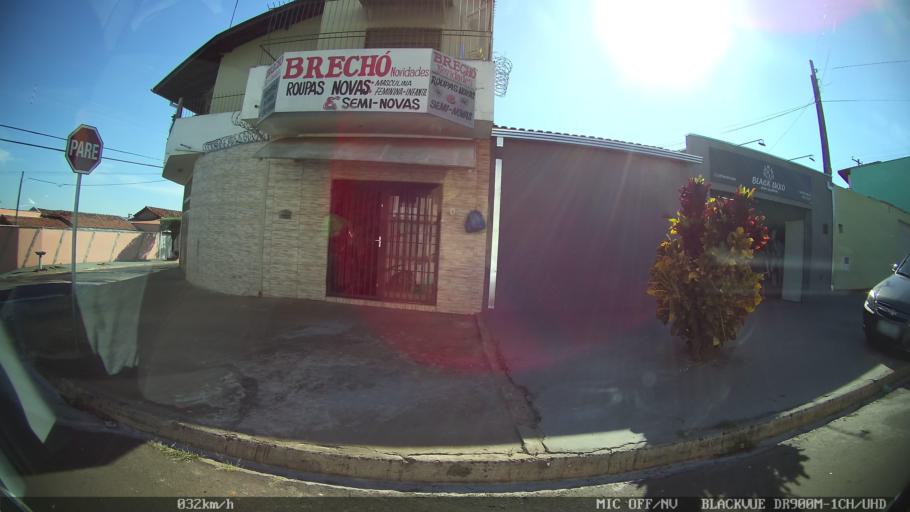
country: BR
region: Sao Paulo
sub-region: Franca
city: Franca
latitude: -20.4901
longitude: -47.4154
